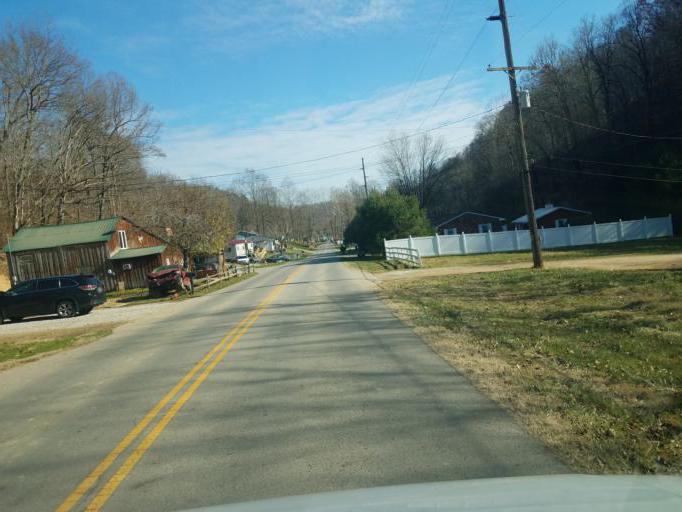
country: US
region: Ohio
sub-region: Scioto County
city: New Boston
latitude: 38.7630
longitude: -82.9513
